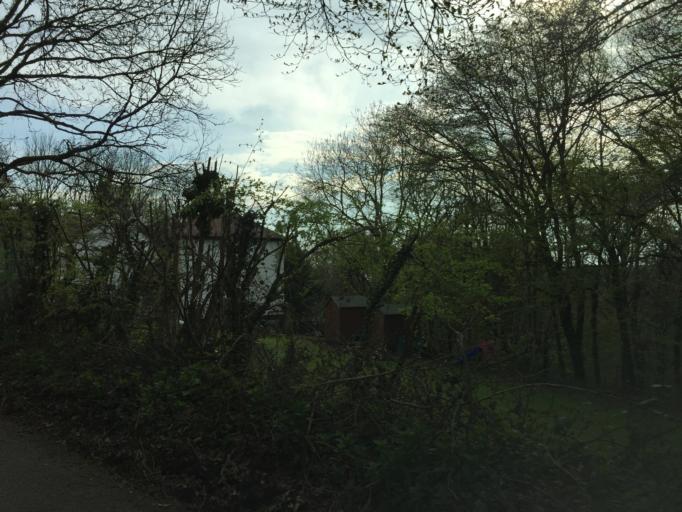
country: GB
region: Wales
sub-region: Caerphilly County Borough
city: Caerphilly
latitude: 51.5458
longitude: -3.2350
